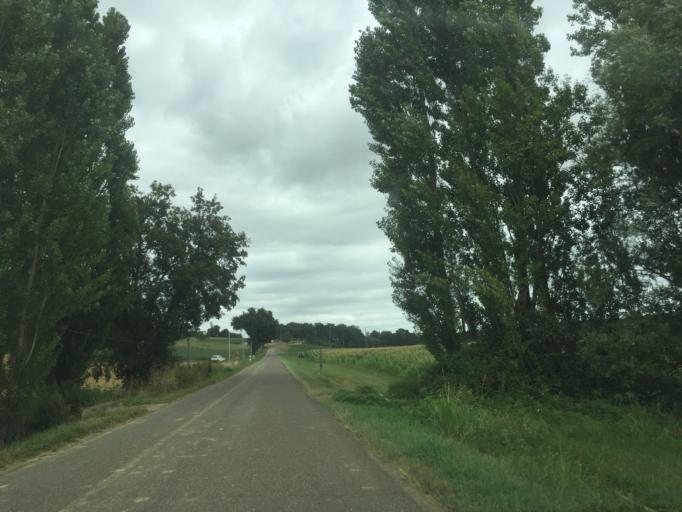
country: FR
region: Midi-Pyrenees
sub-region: Departement du Gers
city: Mirande
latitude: 43.6100
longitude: 0.3398
